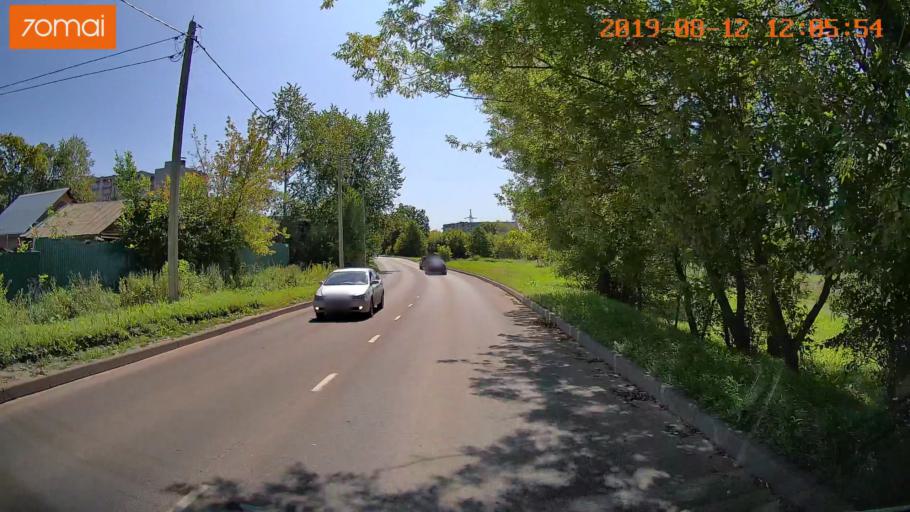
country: RU
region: Ivanovo
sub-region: Gorod Ivanovo
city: Ivanovo
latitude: 56.9914
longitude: 41.0189
